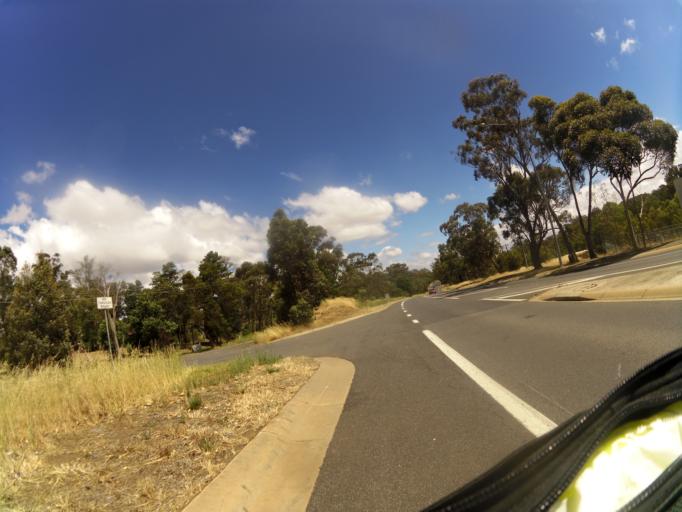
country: AU
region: Victoria
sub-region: Mount Alexander
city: Castlemaine
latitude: -37.0072
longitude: 144.2475
